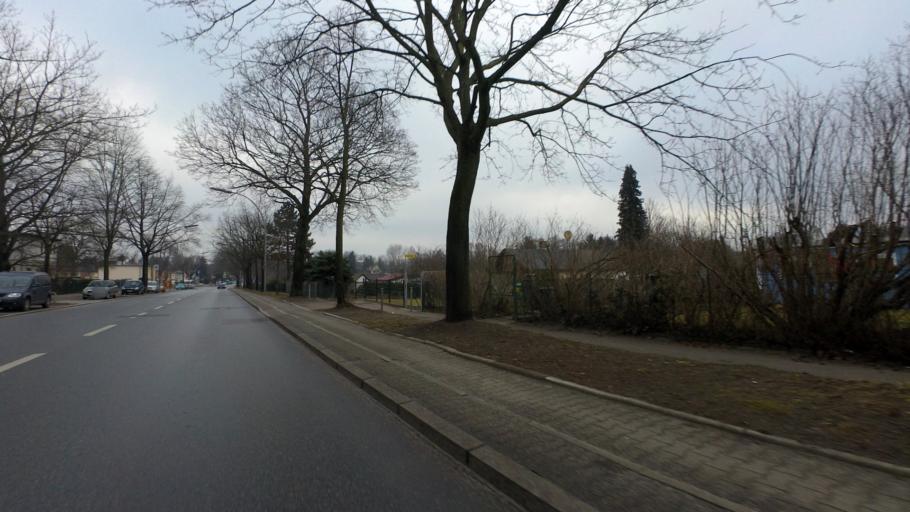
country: DE
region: Berlin
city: Waidmannslust
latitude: 52.6033
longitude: 13.3283
